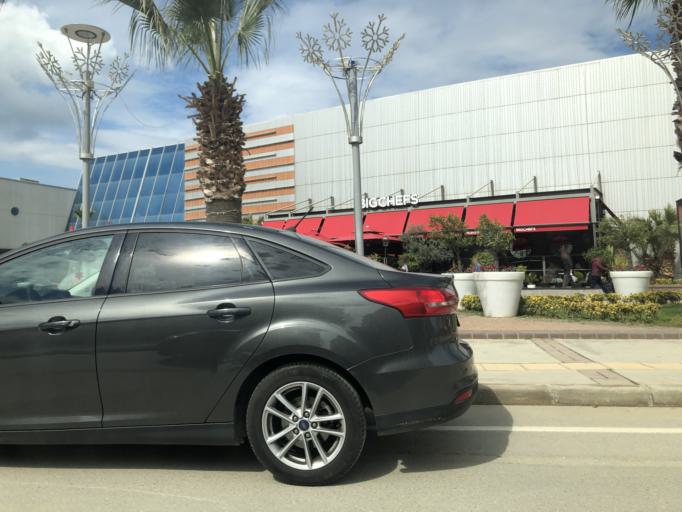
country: TR
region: Izmir
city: Karabaglar
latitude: 38.3945
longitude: 27.0546
